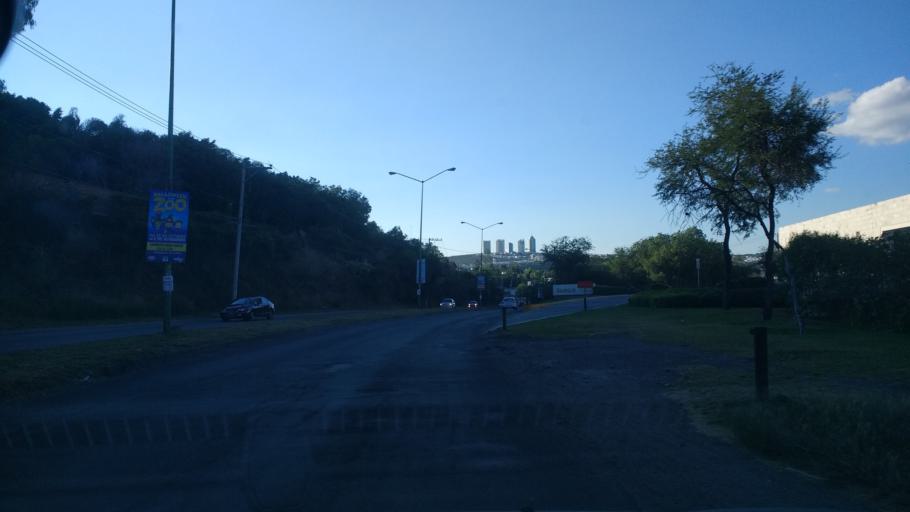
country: MX
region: Guanajuato
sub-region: Leon
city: La Ermita
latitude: 21.1767
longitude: -101.7004
